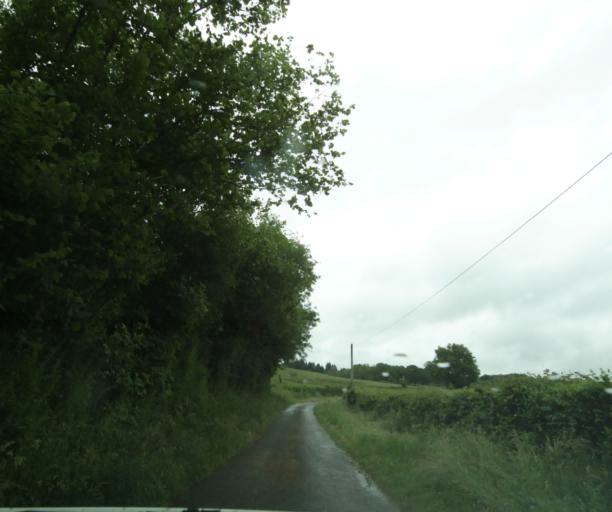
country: FR
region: Bourgogne
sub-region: Departement de Saone-et-Loire
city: Genelard
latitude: 46.5453
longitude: 4.2685
